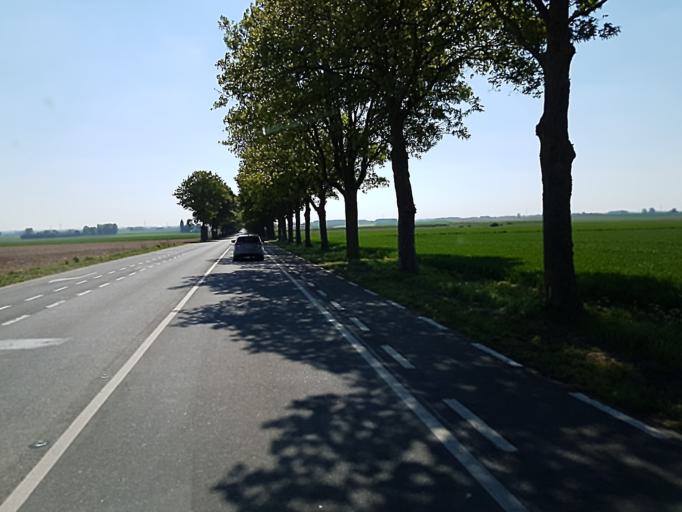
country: BE
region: Wallonia
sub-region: Province du Hainaut
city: Brugelette
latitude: 50.5730
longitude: 3.8720
